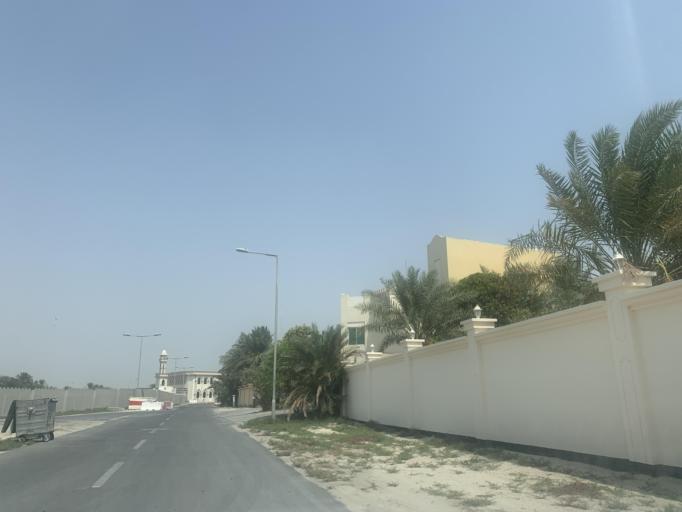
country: BH
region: Central Governorate
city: Madinat Hamad
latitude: 26.1651
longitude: 50.4494
